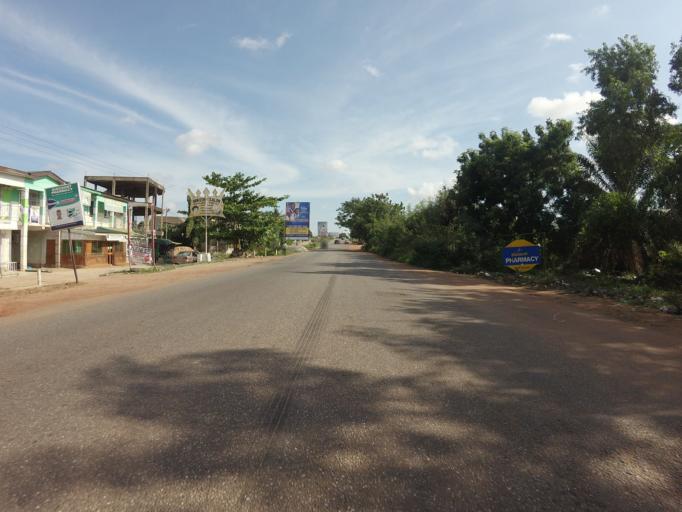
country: GH
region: Greater Accra
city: Medina Estates
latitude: 5.6513
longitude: -0.1692
